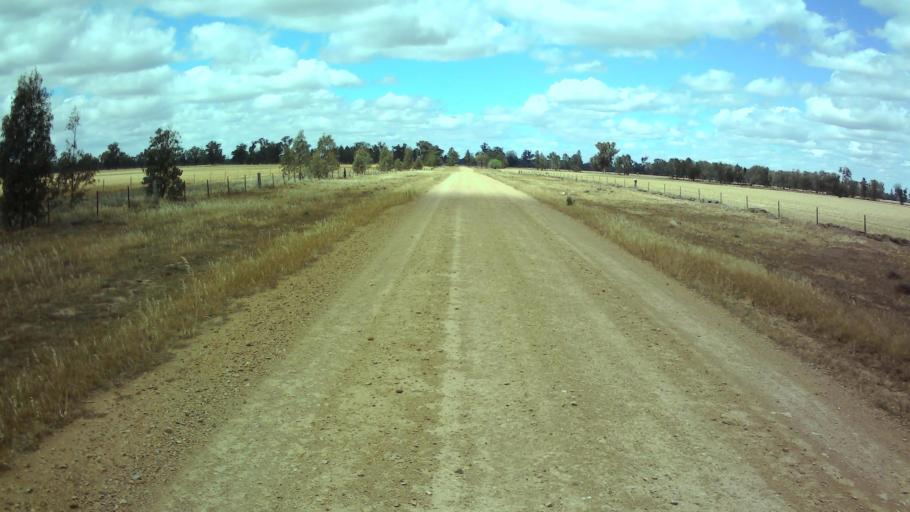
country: AU
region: New South Wales
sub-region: Weddin
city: Grenfell
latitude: -34.0101
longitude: 147.9165
